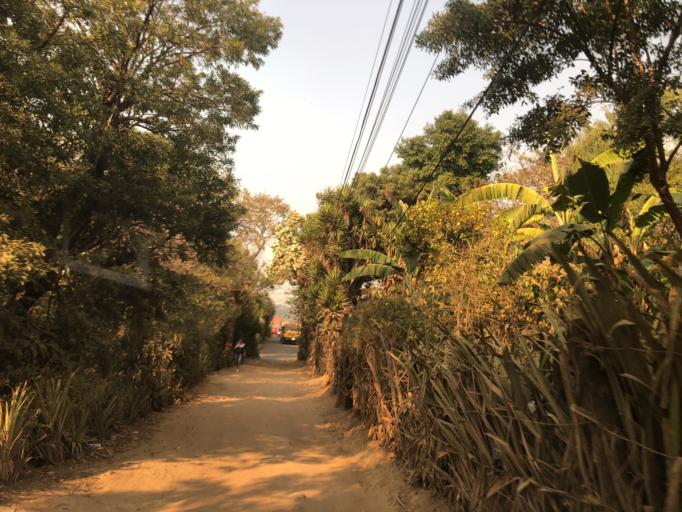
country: GT
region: Guatemala
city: Santa Catarina Pinula
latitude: 14.5386
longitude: -90.5054
